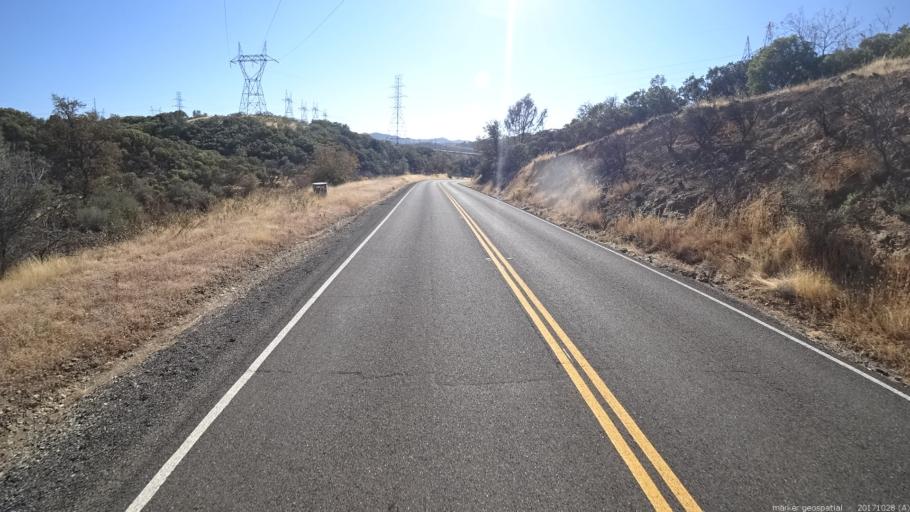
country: US
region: California
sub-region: Shasta County
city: Shasta
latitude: 40.6129
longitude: -122.4415
